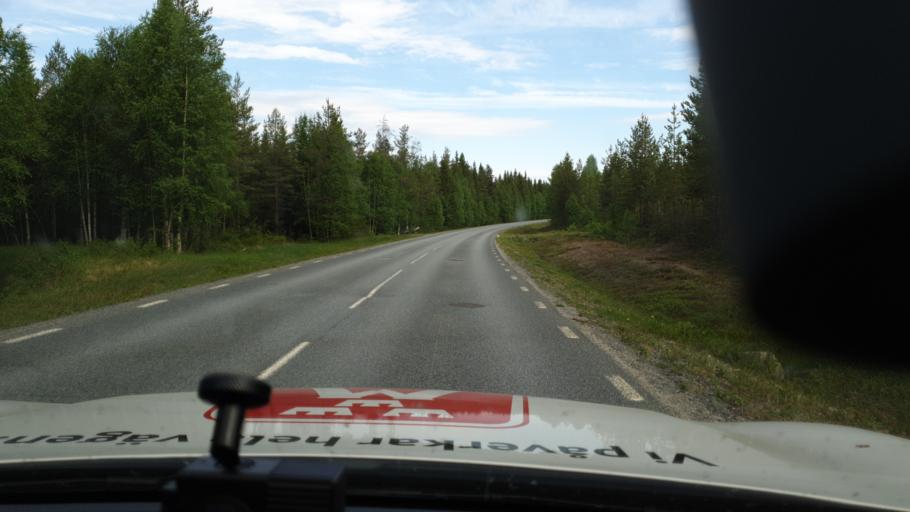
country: SE
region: Vaesterbotten
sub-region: Lycksele Kommun
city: Soderfors
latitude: 65.1297
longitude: 18.2739
